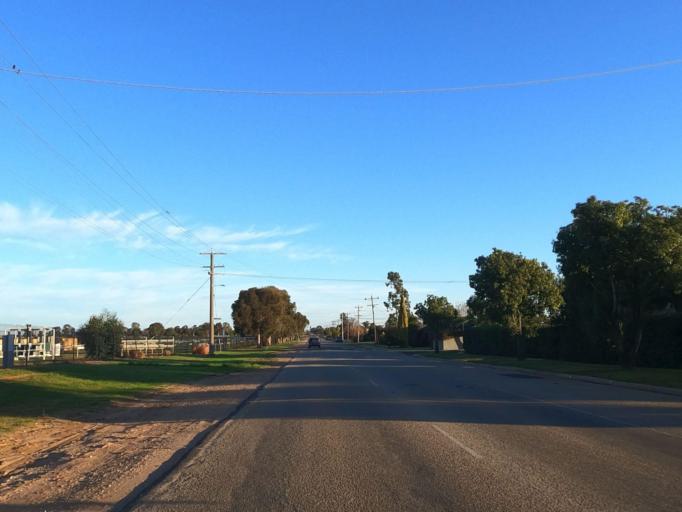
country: AU
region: Victoria
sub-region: Swan Hill
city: Swan Hill
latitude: -35.3487
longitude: 143.5550
